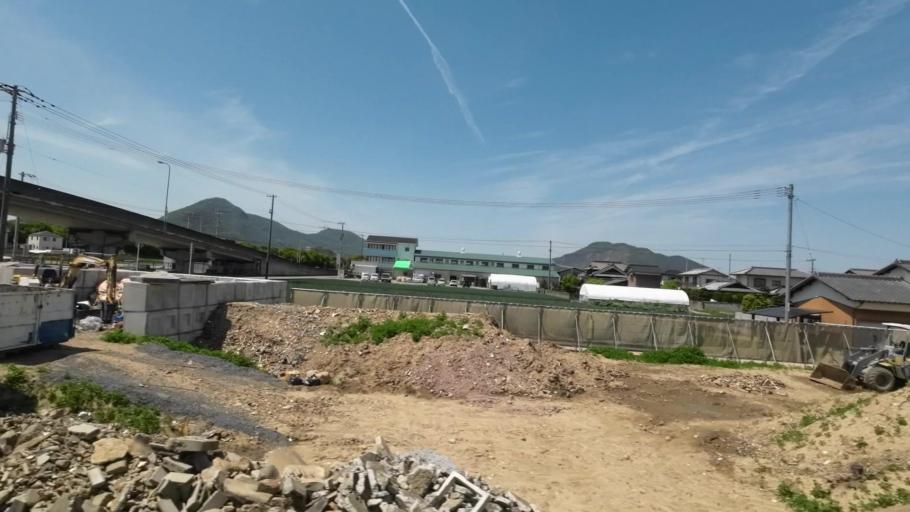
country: JP
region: Kagawa
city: Marugame
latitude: 34.2447
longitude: 133.7799
